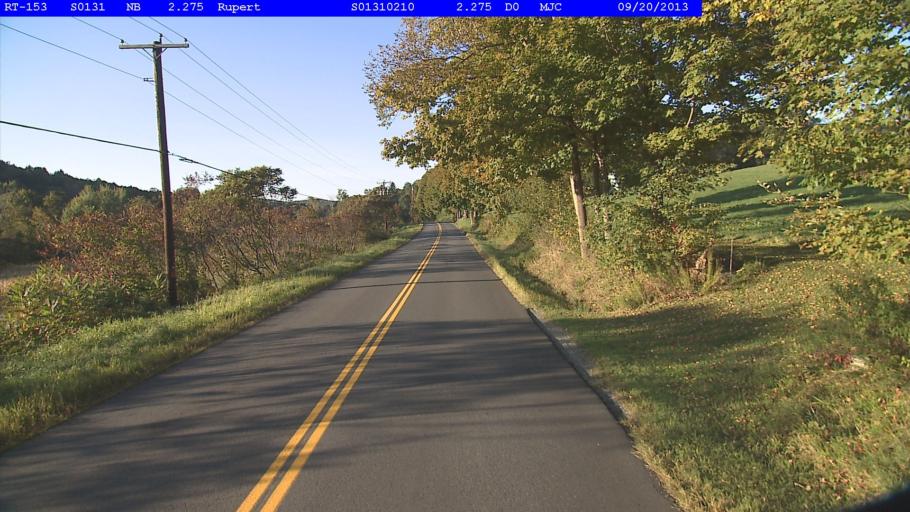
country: US
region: New York
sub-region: Washington County
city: Granville
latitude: 43.2878
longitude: -73.2391
